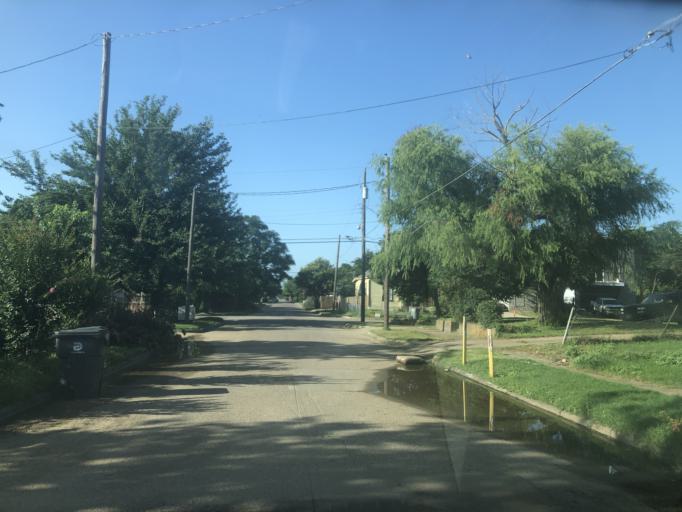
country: US
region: Texas
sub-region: Dallas County
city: Dallas
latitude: 32.7918
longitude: -96.8534
